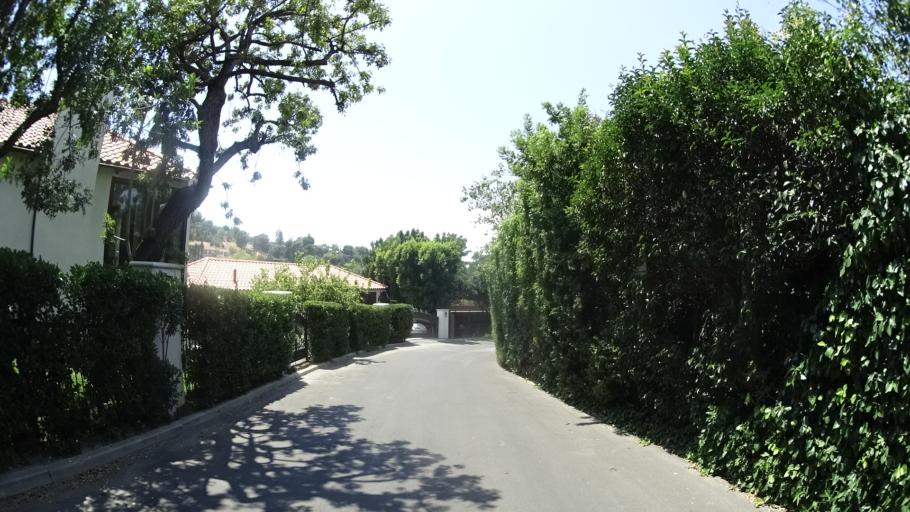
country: US
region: California
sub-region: Los Angeles County
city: Sherman Oaks
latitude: 34.1392
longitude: -118.4215
